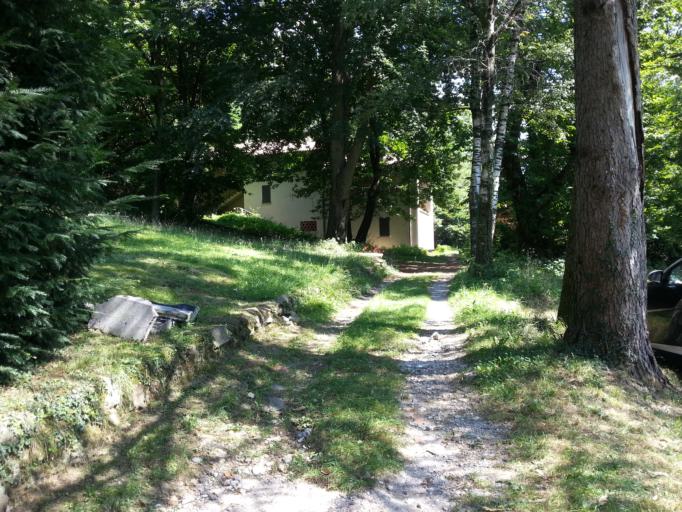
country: IT
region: Lombardy
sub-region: Provincia di Lecco
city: Ballabio
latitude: 45.8721
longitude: 9.4112
